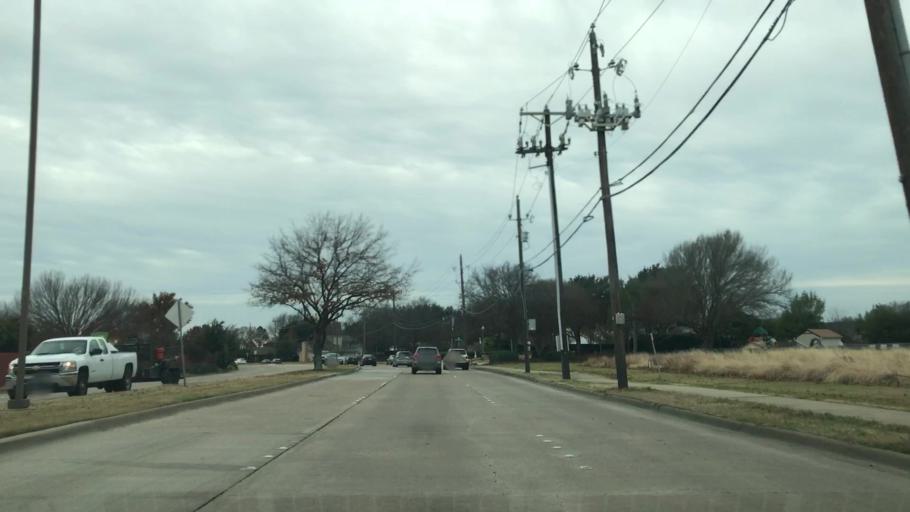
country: US
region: Texas
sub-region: Dallas County
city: Carrollton
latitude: 33.0177
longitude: -96.8860
